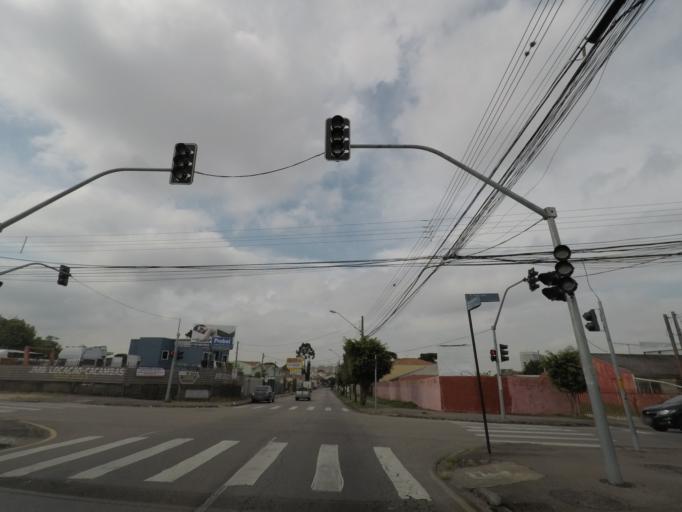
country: BR
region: Parana
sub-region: Curitiba
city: Curitiba
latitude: -25.4962
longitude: -49.2839
